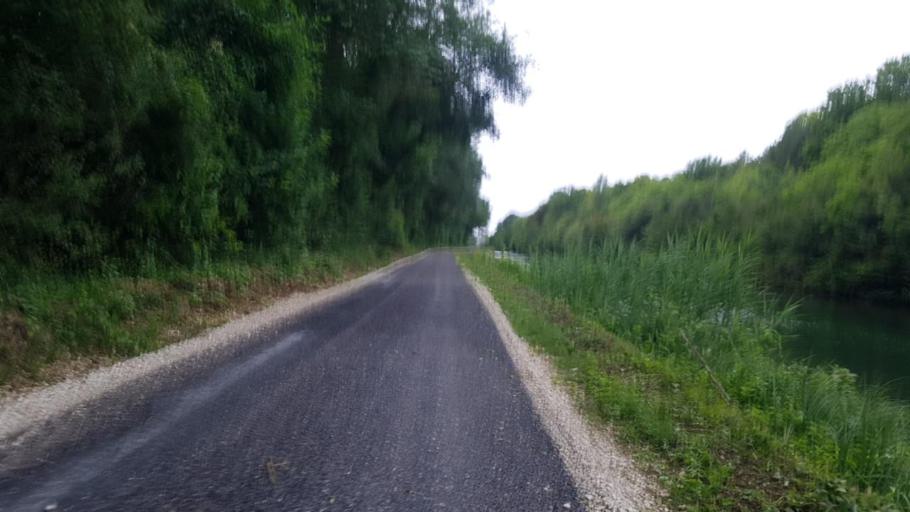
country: FR
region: Champagne-Ardenne
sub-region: Departement de la Marne
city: Sarry
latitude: 48.8410
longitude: 4.5012
